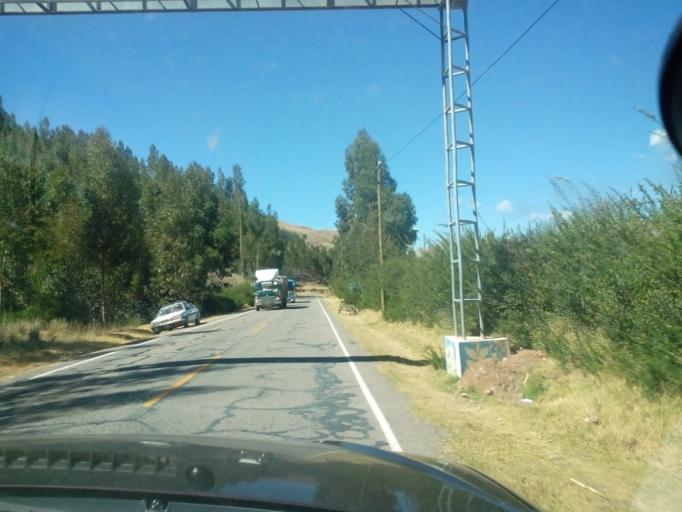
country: PE
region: Cusco
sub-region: Provincia de Canchis
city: Combapata
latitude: -14.1058
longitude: -71.4222
